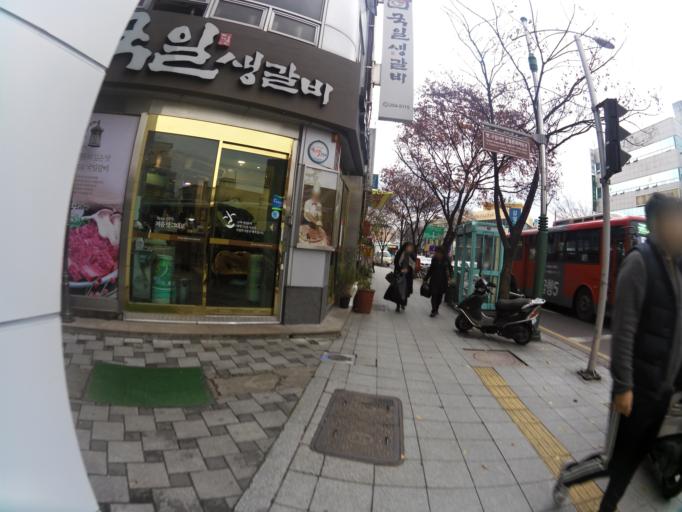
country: KR
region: Daegu
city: Daegu
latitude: 35.8704
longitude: 128.5847
